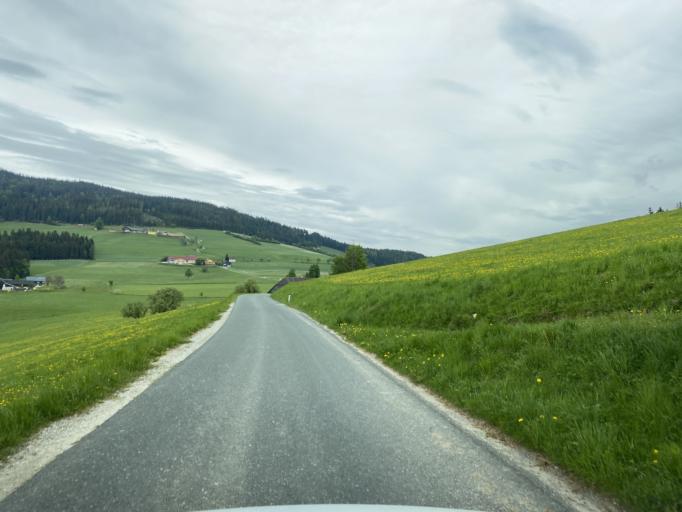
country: AT
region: Styria
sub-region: Politischer Bezirk Weiz
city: Gschaid bei Birkfeld
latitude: 47.3369
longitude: 15.7384
